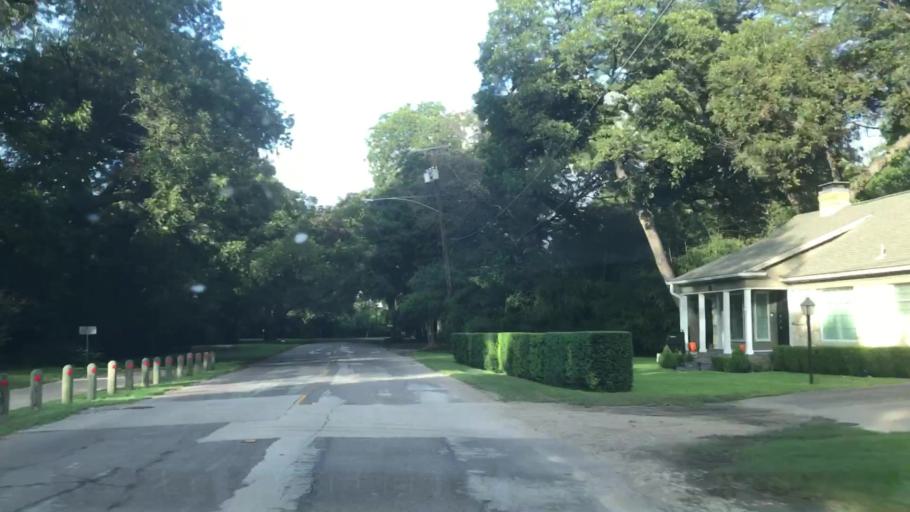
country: US
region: Texas
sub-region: Dallas County
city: Dallas
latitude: 32.7641
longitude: -96.8407
